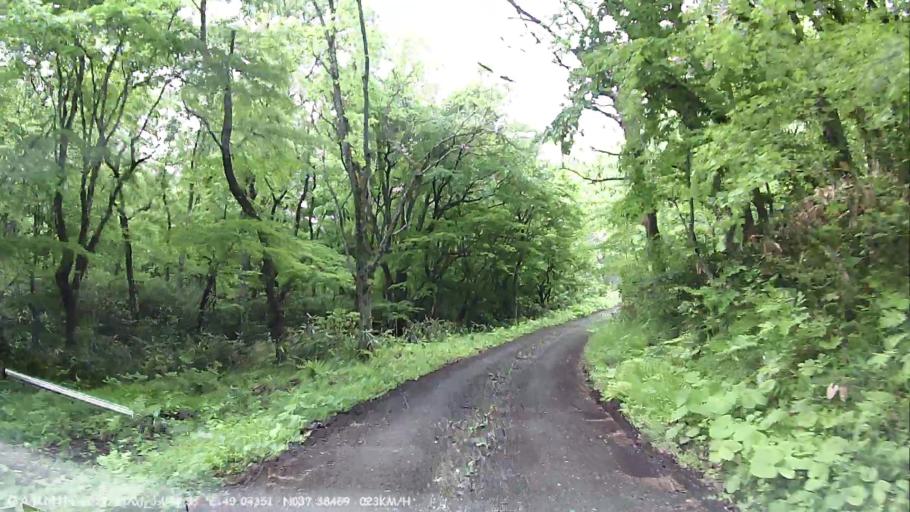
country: JP
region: Fukushima
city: Inawashiro
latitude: 37.3846
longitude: 140.0435
